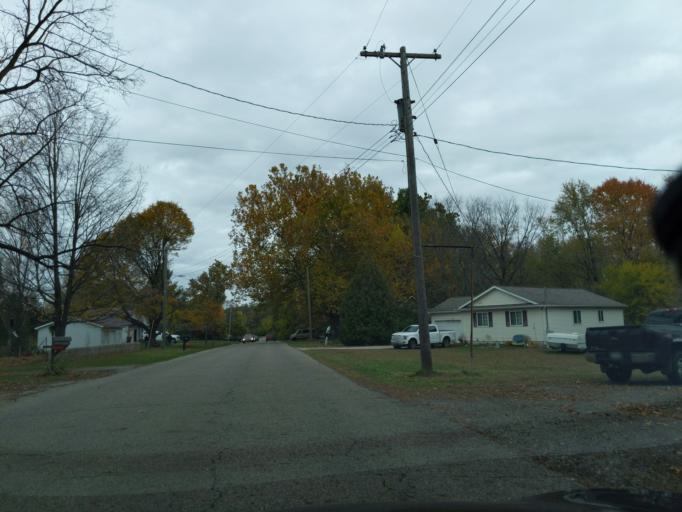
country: US
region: Michigan
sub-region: Eaton County
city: Eaton Rapids
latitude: 42.5211
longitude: -84.6457
